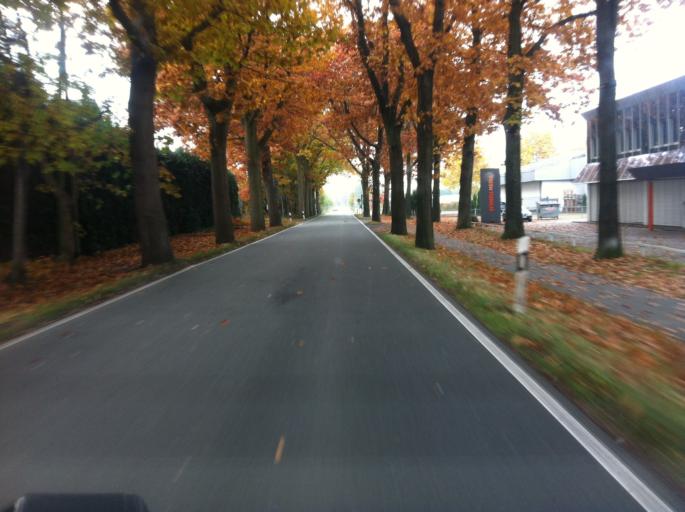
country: DE
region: North Rhine-Westphalia
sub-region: Regierungsbezirk Munster
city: Vreden
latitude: 52.0207
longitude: 6.8038
